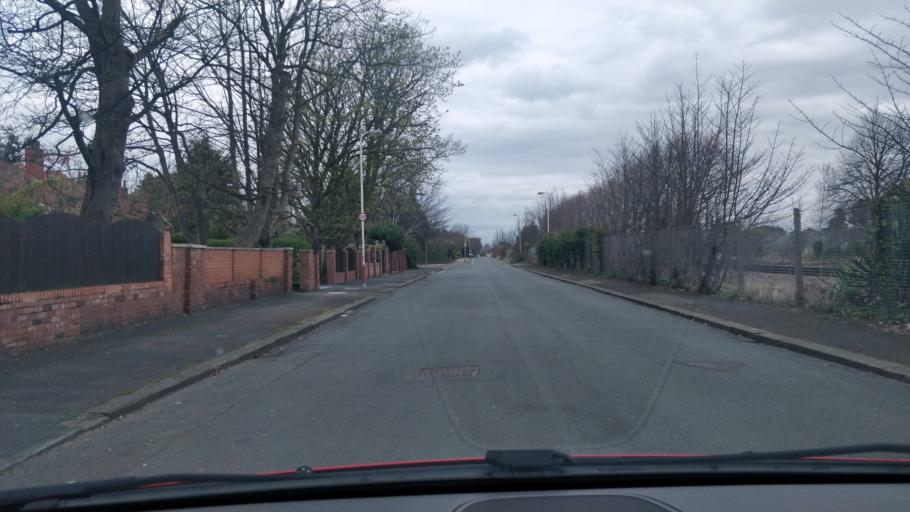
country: GB
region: England
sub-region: Sefton
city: Southport
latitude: 53.6050
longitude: -3.0402
